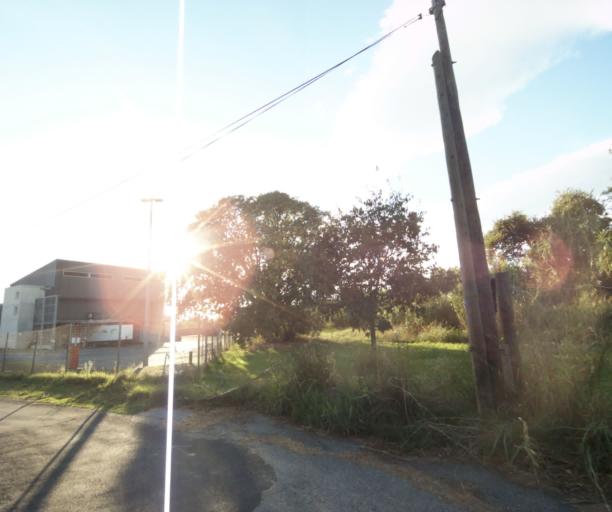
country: FR
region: Languedoc-Roussillon
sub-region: Departement des Pyrenees-Orientales
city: Elne
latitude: 42.5850
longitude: 2.9904
